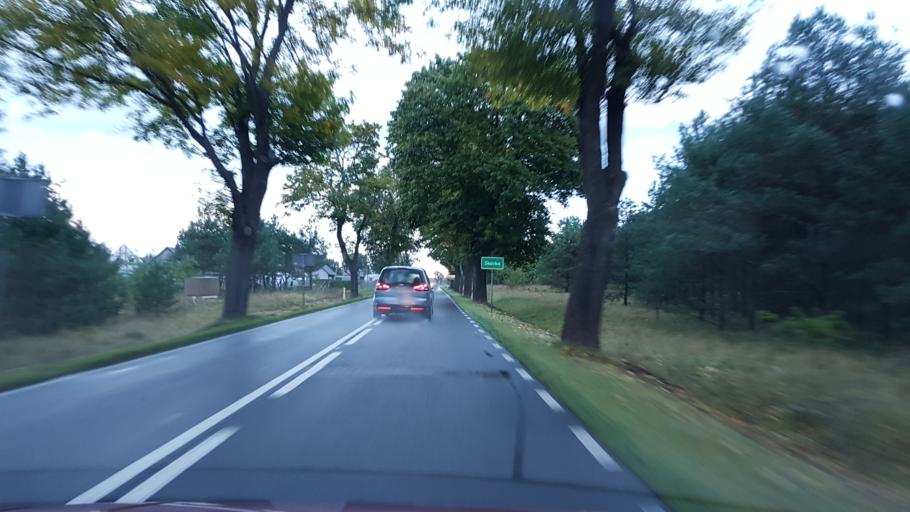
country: PL
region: Greater Poland Voivodeship
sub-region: Powiat pilski
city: Smilowo
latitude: 53.2164
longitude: 16.8645
